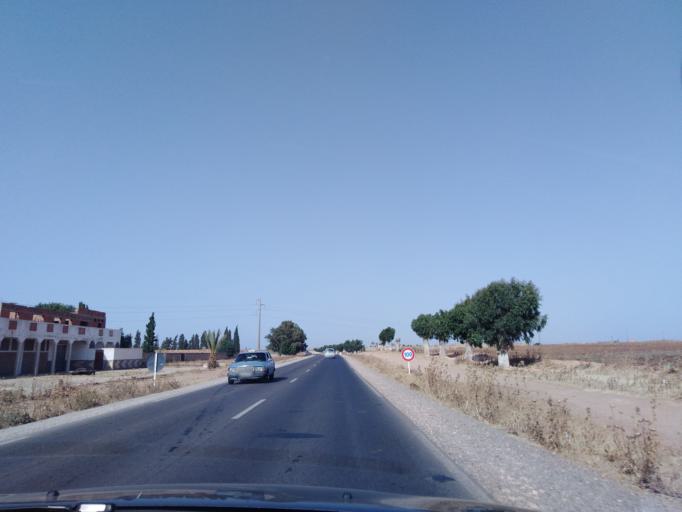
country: MA
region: Doukkala-Abda
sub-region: Safi
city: Safi
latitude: 32.2596
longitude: -8.9673
